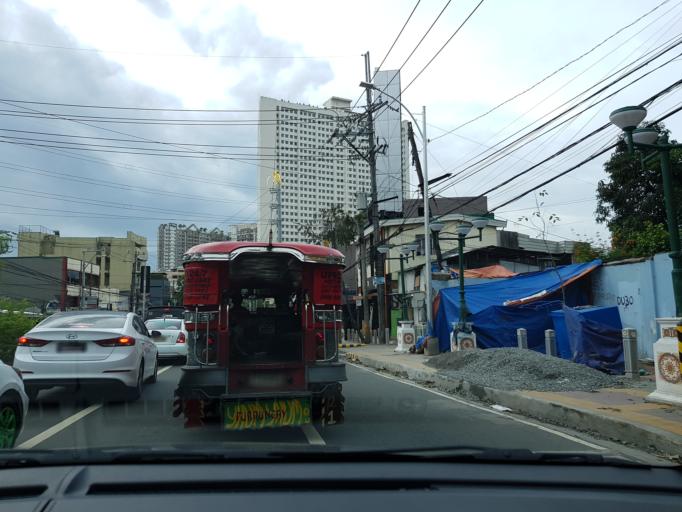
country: PH
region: Calabarzon
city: Del Monte
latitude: 14.6278
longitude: 121.0337
